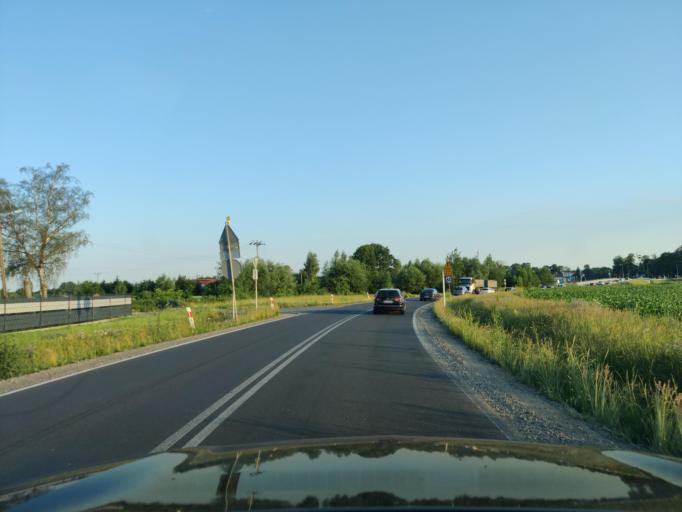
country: PL
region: Masovian Voivodeship
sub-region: Powiat plonski
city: Baboszewo
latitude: 52.7077
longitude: 20.3384
